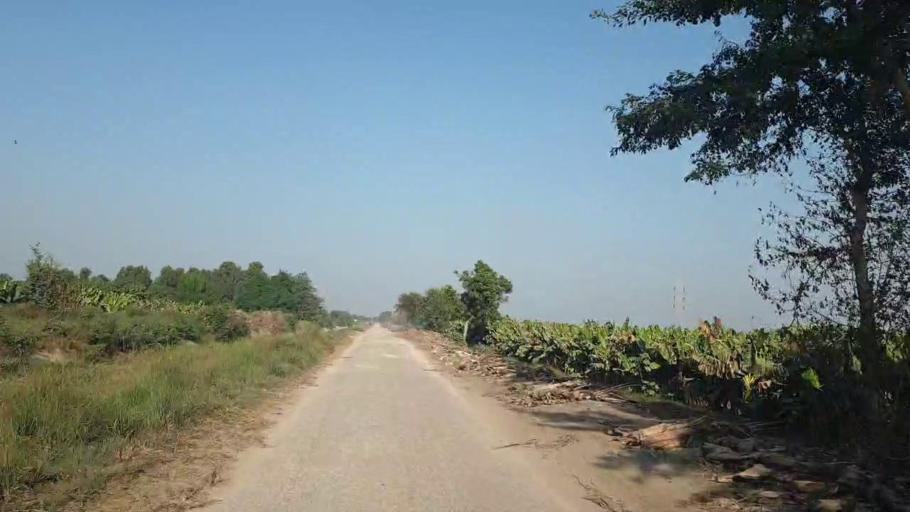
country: PK
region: Sindh
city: Matiari
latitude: 25.5349
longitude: 68.4382
